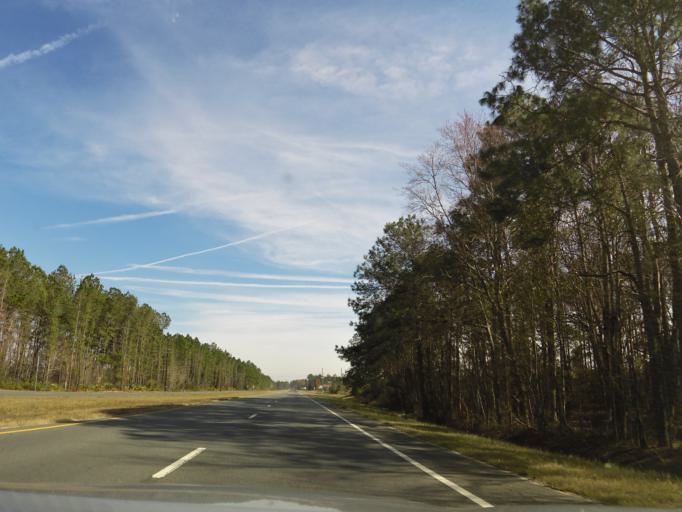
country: US
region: Georgia
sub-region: Brantley County
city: Nahunta
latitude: 31.2000
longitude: -82.0084
